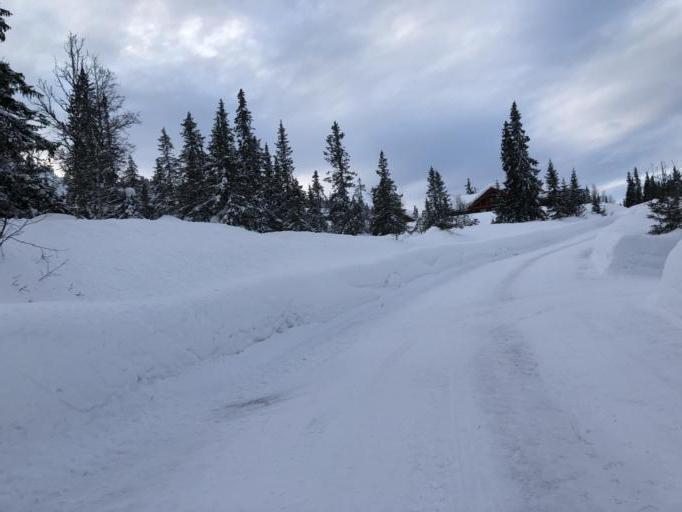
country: NO
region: Oppland
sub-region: Gausdal
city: Segalstad bru
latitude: 61.3285
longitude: 10.0539
